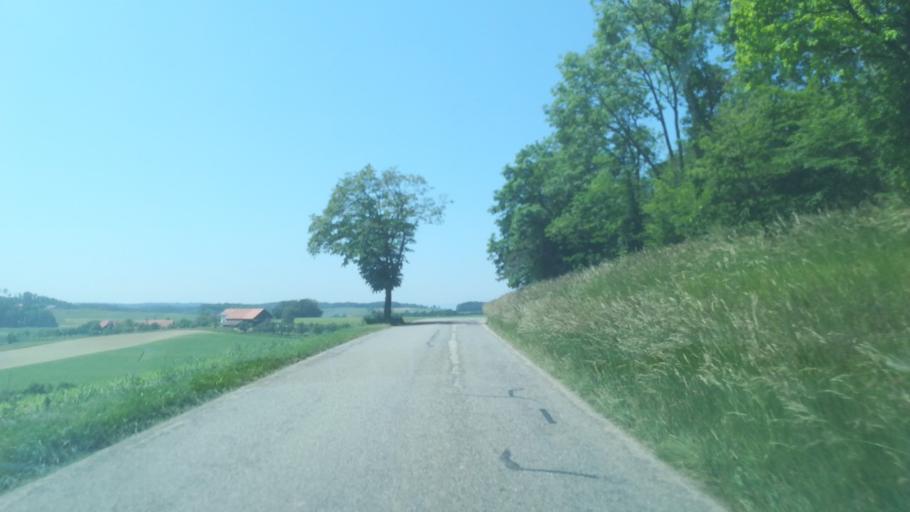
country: CH
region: Thurgau
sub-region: Frauenfeld District
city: Pfyn
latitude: 47.6255
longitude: 8.9327
